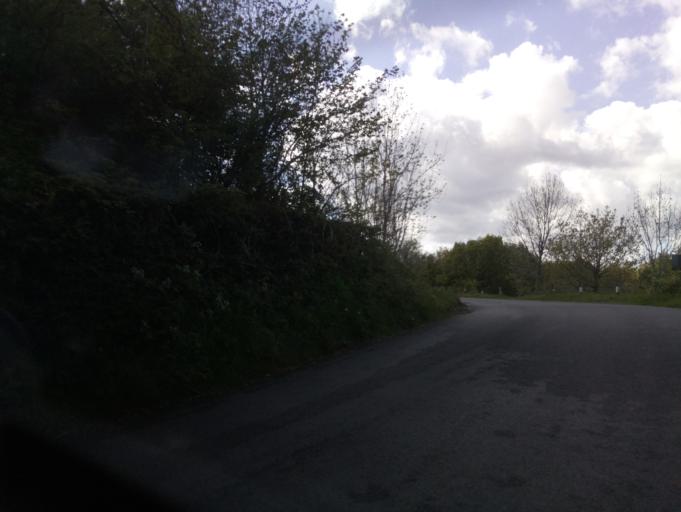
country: GB
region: Wales
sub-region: Caerphilly County Borough
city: Bedwas
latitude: 51.5724
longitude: -3.1742
